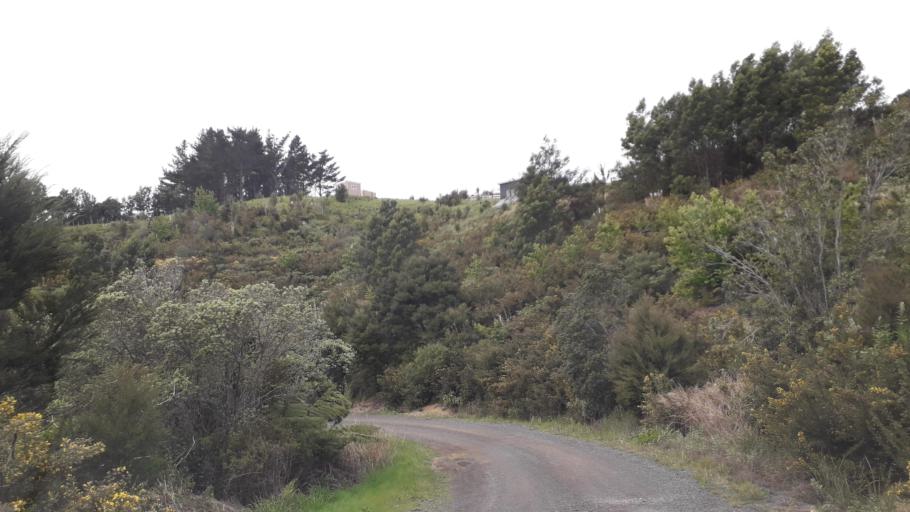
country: NZ
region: Northland
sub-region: Far North District
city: Paihia
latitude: -35.2823
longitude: 174.1848
